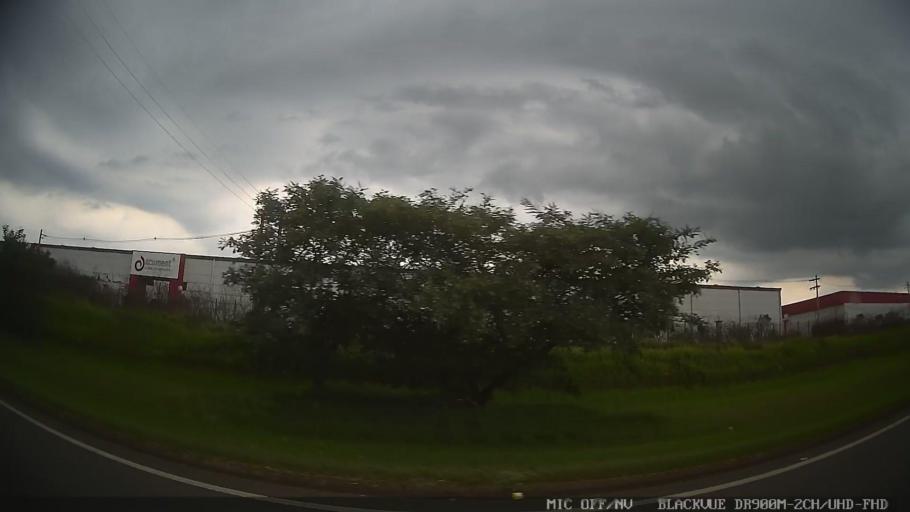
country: BR
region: Sao Paulo
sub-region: Jarinu
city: Jarinu
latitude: -23.0436
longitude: -46.6755
